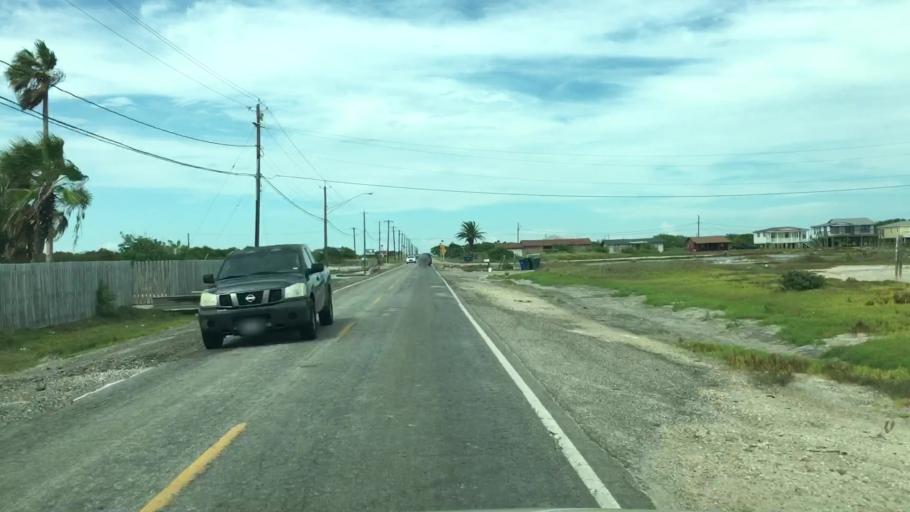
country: US
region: Texas
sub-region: Nueces County
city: Corpus Christi
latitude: 27.6414
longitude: -97.2861
